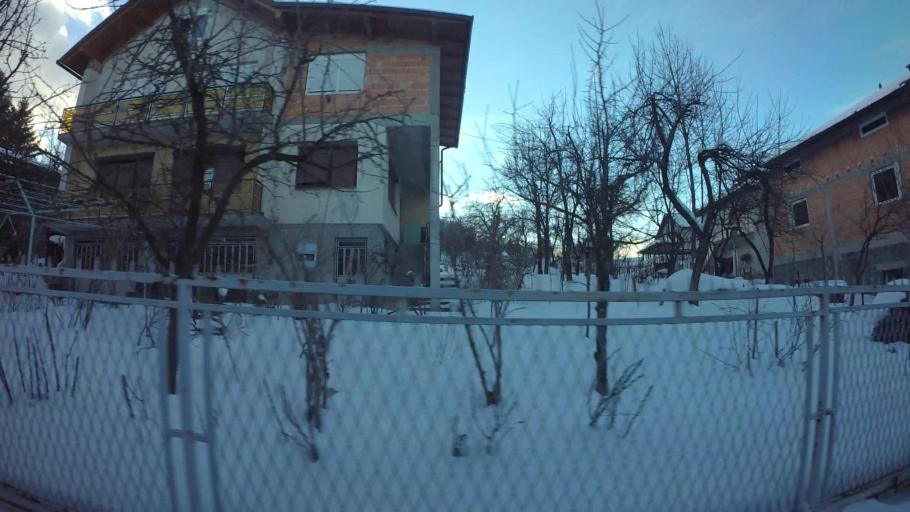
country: BA
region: Federation of Bosnia and Herzegovina
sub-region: Kanton Sarajevo
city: Sarajevo
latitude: 43.8075
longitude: 18.3577
